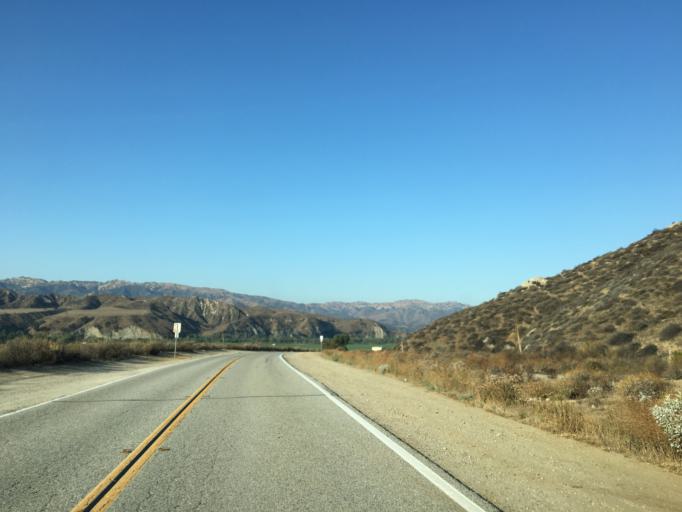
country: US
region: California
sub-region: Los Angeles County
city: Valencia
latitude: 34.4291
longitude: -118.6309
